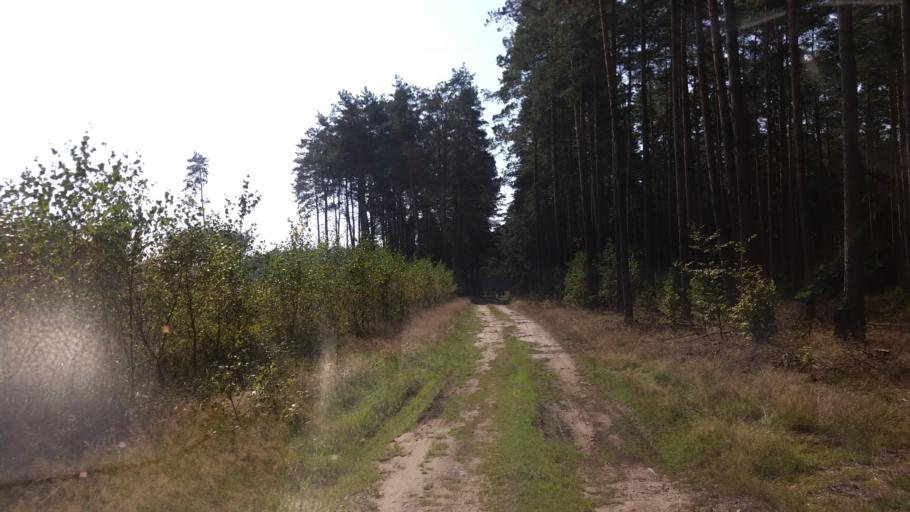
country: PL
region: West Pomeranian Voivodeship
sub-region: Powiat drawski
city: Kalisz Pomorski
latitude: 53.2035
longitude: 15.8946
